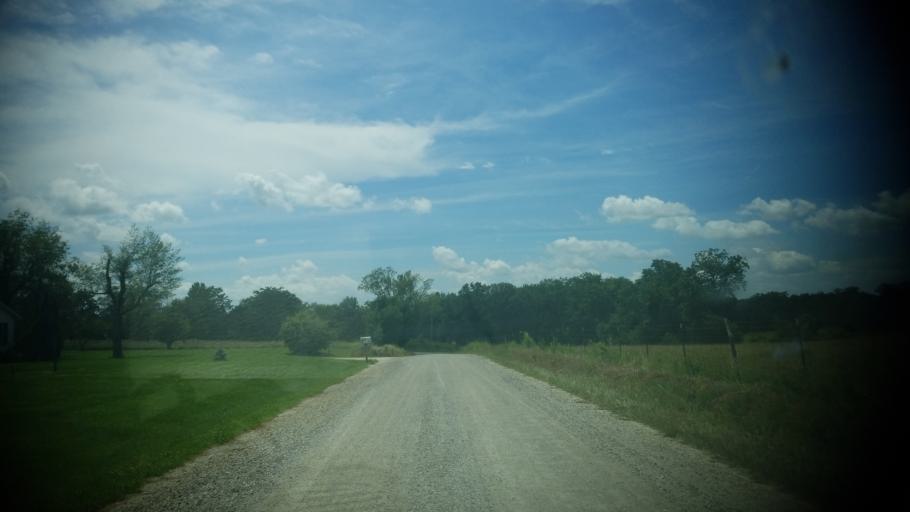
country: US
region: Missouri
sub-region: Audrain County
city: Vandalia
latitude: 39.3092
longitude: -91.3432
